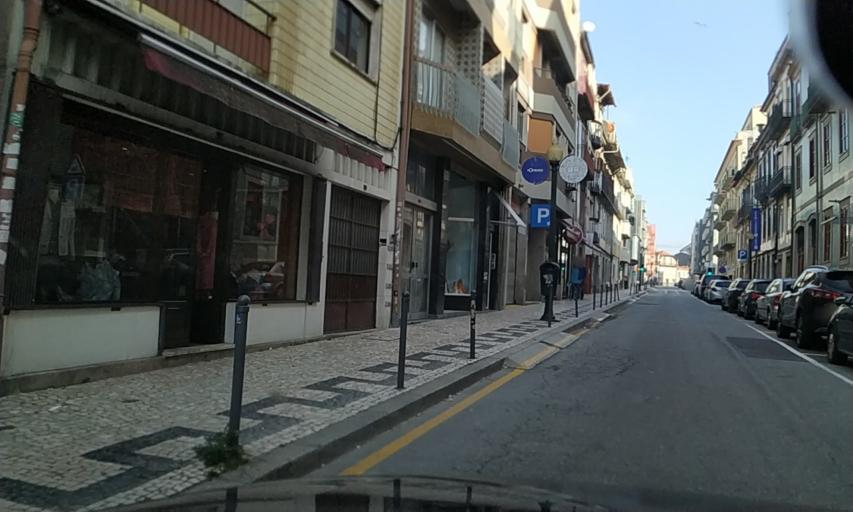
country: PT
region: Porto
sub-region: Porto
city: Porto
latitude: 41.1498
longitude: -8.6209
